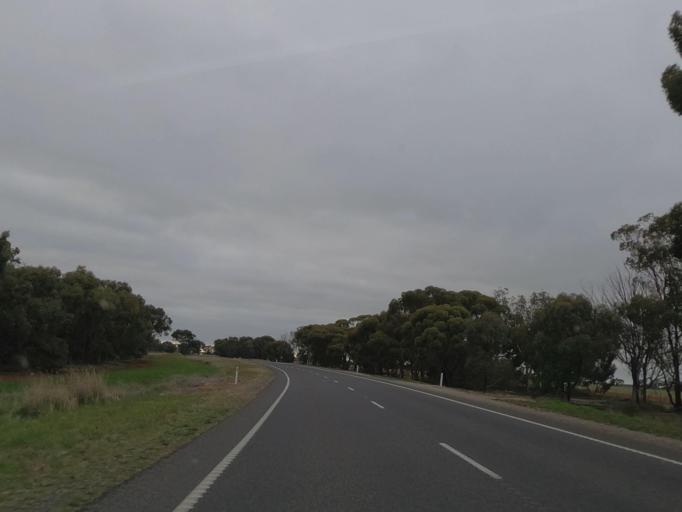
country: AU
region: Victoria
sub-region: Greater Bendigo
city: Long Gully
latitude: -36.0624
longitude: 143.9471
